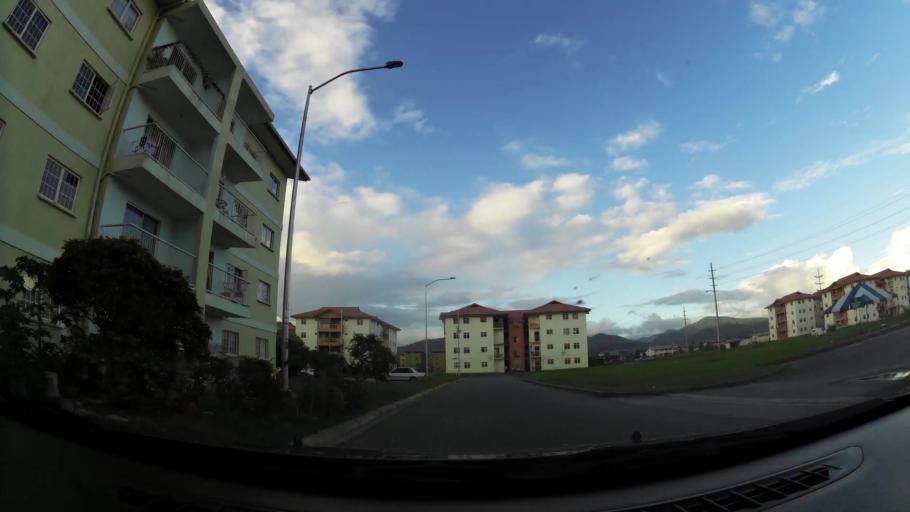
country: TT
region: Tunapuna/Piarco
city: Arouca
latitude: 10.6133
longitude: -61.3546
